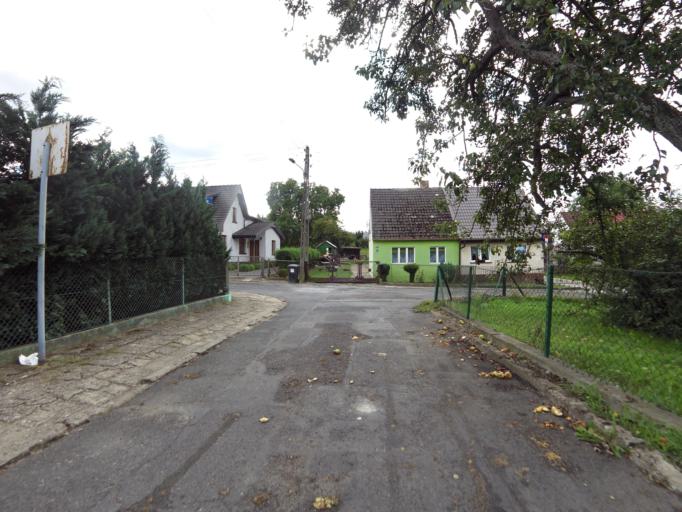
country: PL
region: West Pomeranian Voivodeship
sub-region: Powiat mysliborski
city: Mysliborz
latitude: 52.9164
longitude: 14.8552
